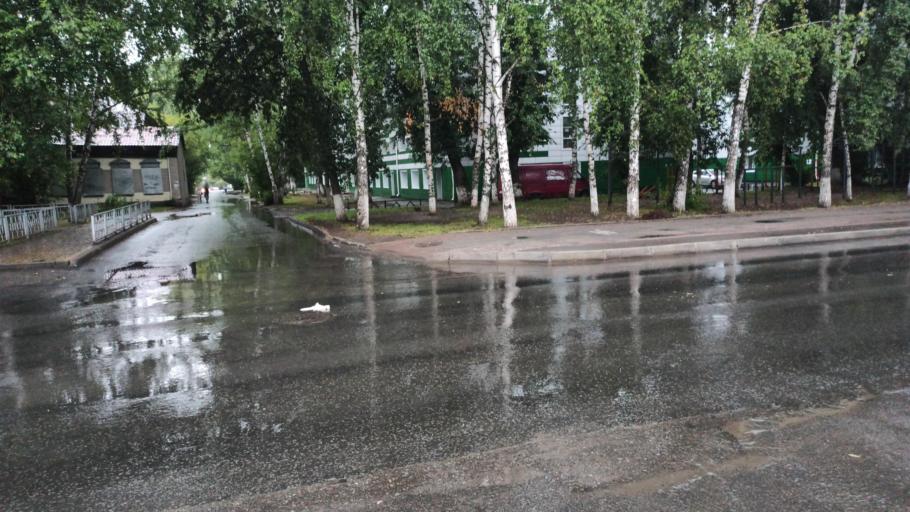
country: RU
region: Tomsk
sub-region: Tomskiy Rayon
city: Tomsk
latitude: 56.4614
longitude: 84.9628
